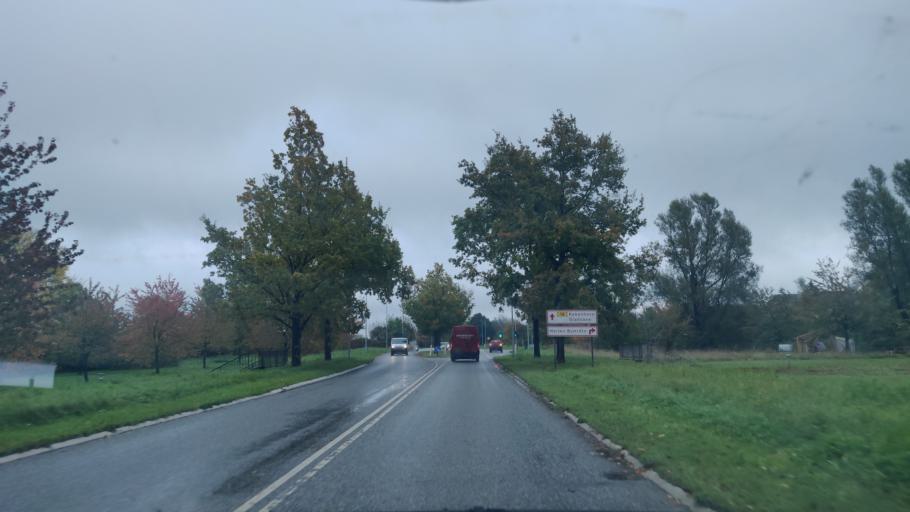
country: DK
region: Capital Region
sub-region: Herlev Kommune
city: Herlev
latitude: 55.7447
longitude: 12.4243
